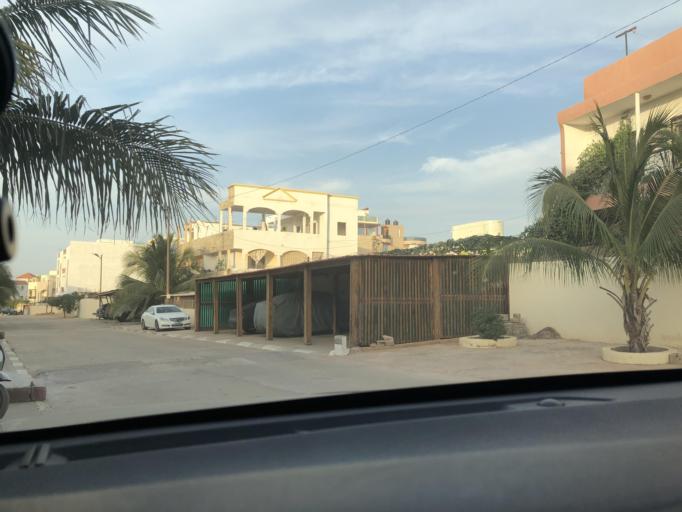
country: SN
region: Dakar
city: Mermoz Boabab
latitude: 14.7313
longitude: -17.5020
